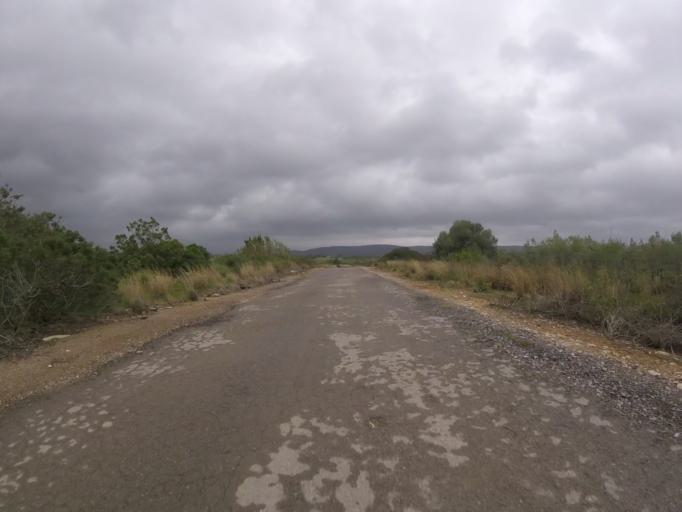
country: ES
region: Valencia
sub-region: Provincia de Castello
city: Alcala de Xivert
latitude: 40.2816
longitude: 0.2243
